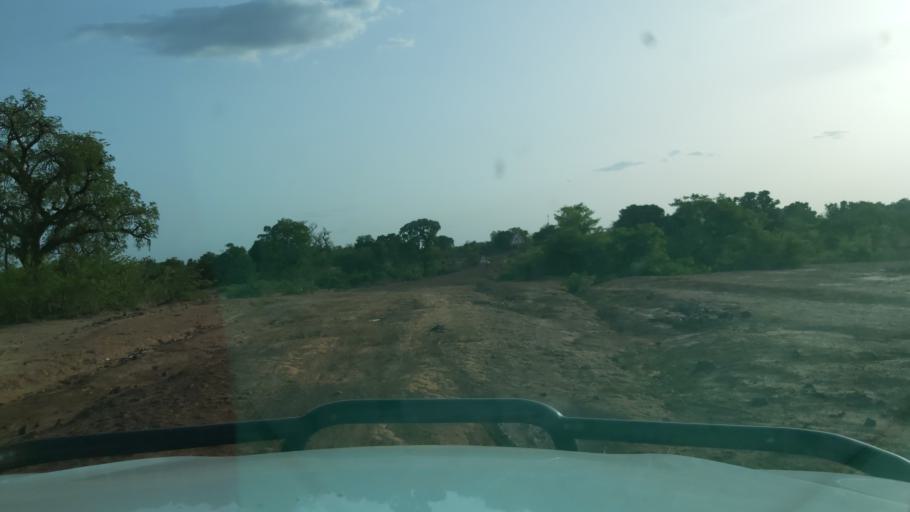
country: ML
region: Koulikoro
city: Kolokani
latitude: 13.2055
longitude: -7.9187
